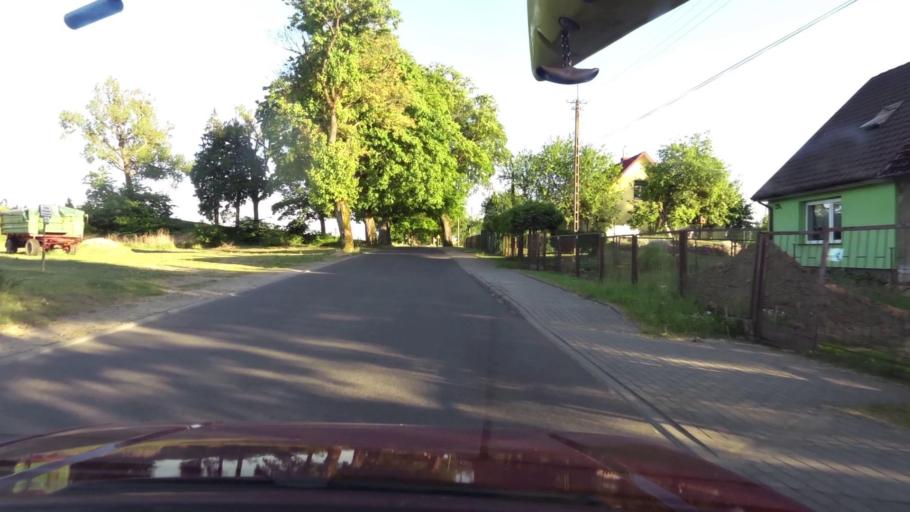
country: PL
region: West Pomeranian Voivodeship
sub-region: Powiat szczecinecki
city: Bialy Bor
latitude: 53.9482
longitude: 16.7850
